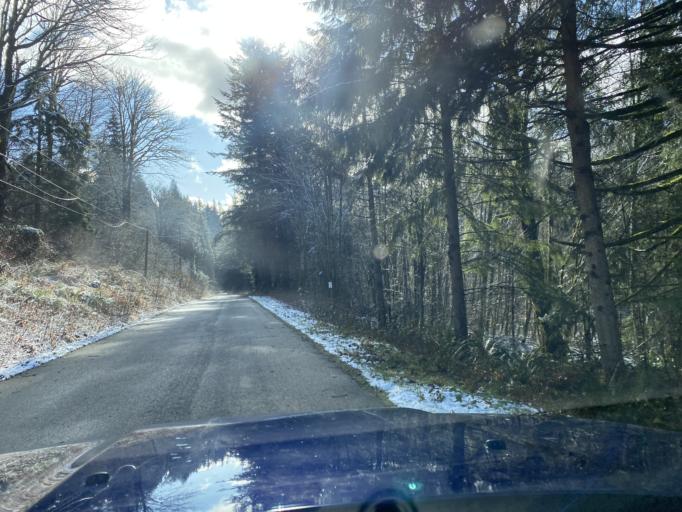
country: US
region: Washington
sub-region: King County
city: Snoqualmie
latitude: 47.5088
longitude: -121.8739
